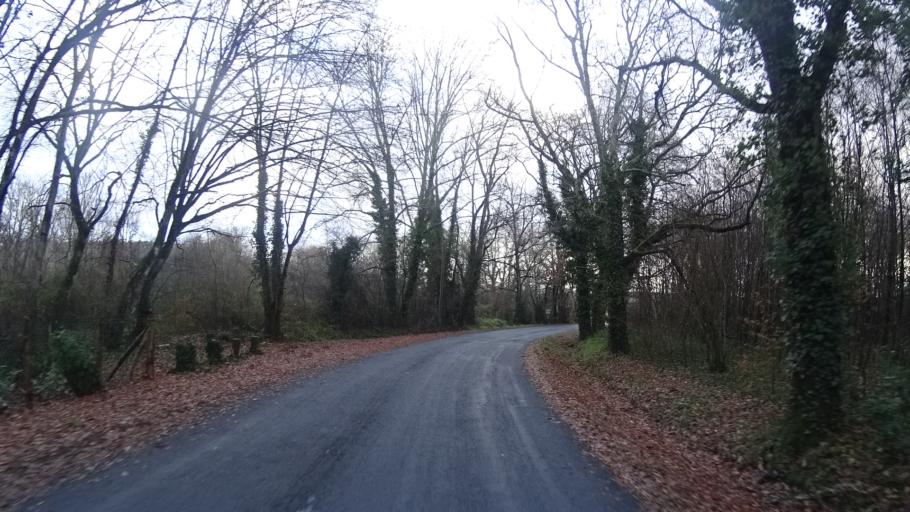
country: FR
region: Aquitaine
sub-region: Departement de la Dordogne
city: Bassillac
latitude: 45.2028
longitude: 0.8056
